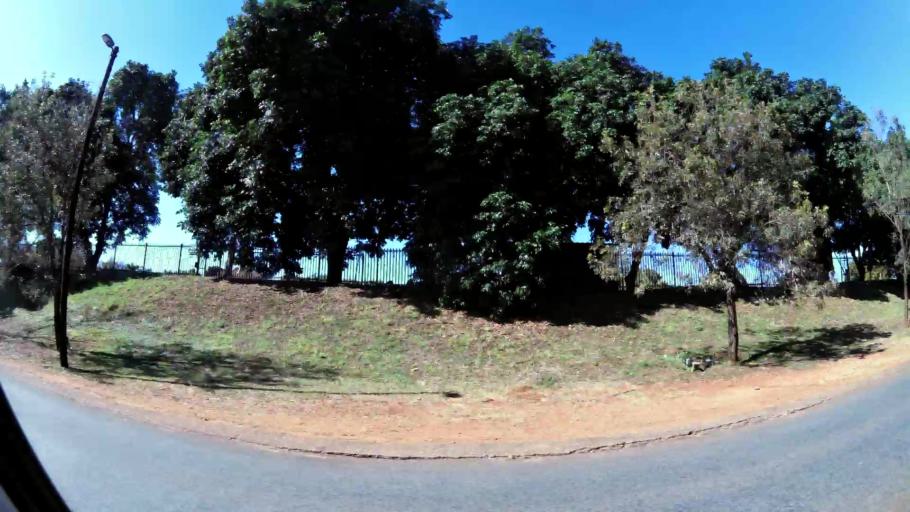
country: ZA
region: Limpopo
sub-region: Mopani District Municipality
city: Tzaneen
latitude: -23.8301
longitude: 30.1535
